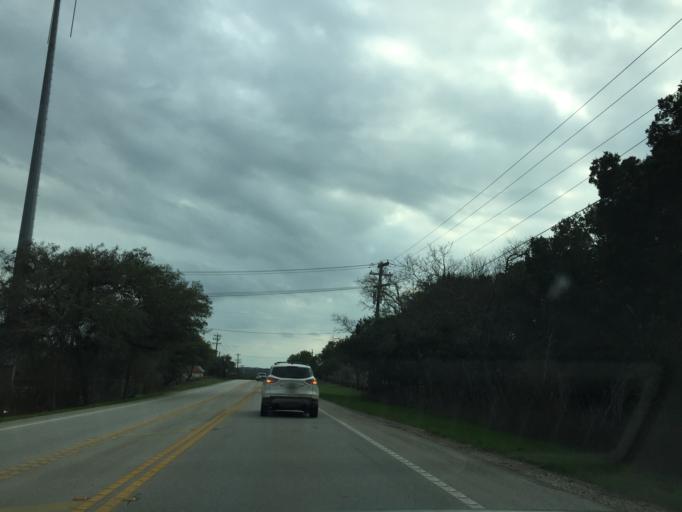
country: US
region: Texas
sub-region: Hays County
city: Dripping Springs
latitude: 30.1349
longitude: -98.0084
